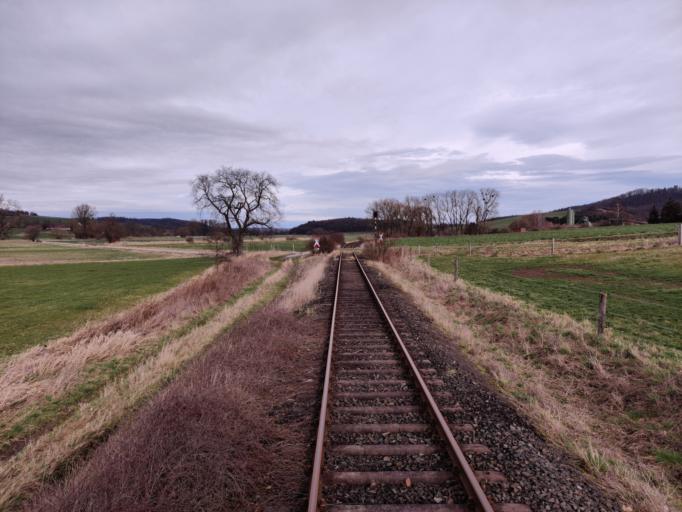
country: DE
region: Lower Saxony
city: Bockenem
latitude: 52.0487
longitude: 10.1298
